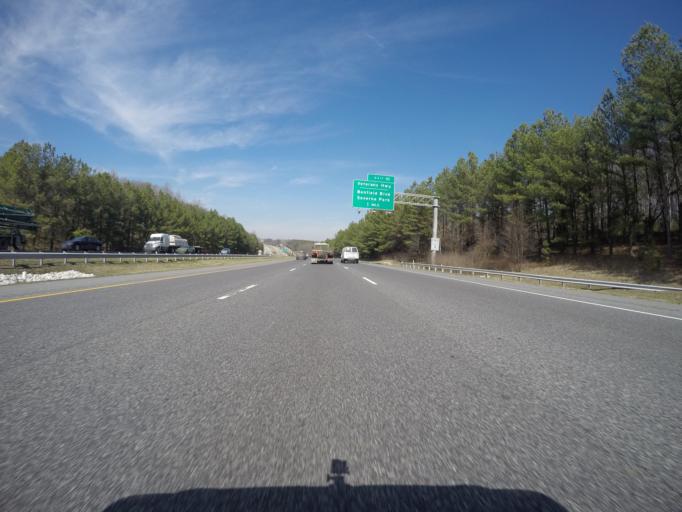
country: US
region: Maryland
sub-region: Anne Arundel County
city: Gambrills
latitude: 39.0747
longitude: -76.6304
